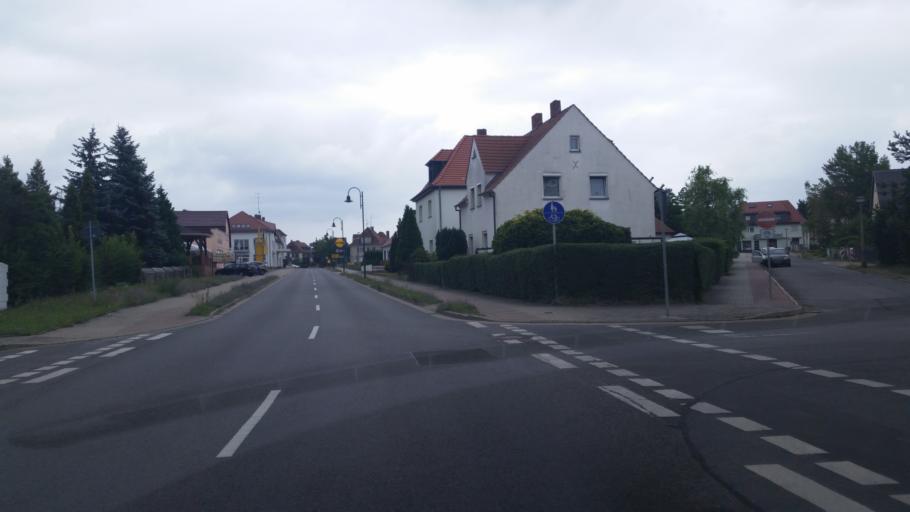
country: DE
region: Saxony
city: Bernsdorf
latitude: 51.4607
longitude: 14.0953
